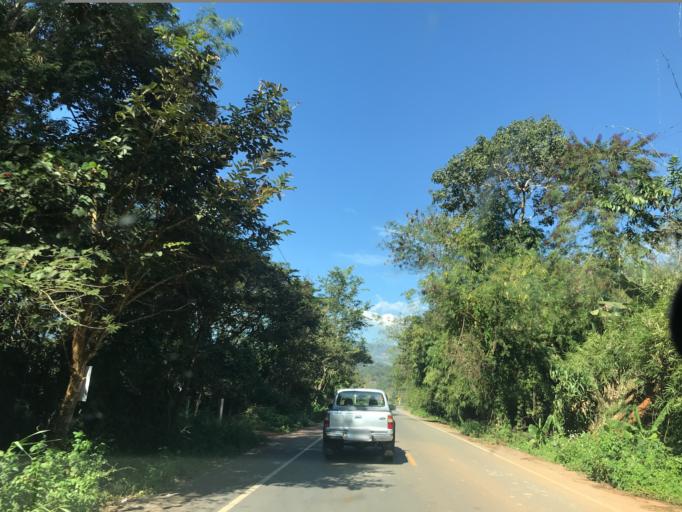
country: TH
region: Chiang Rai
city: Mae Lao
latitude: 19.8071
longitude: 99.6471
